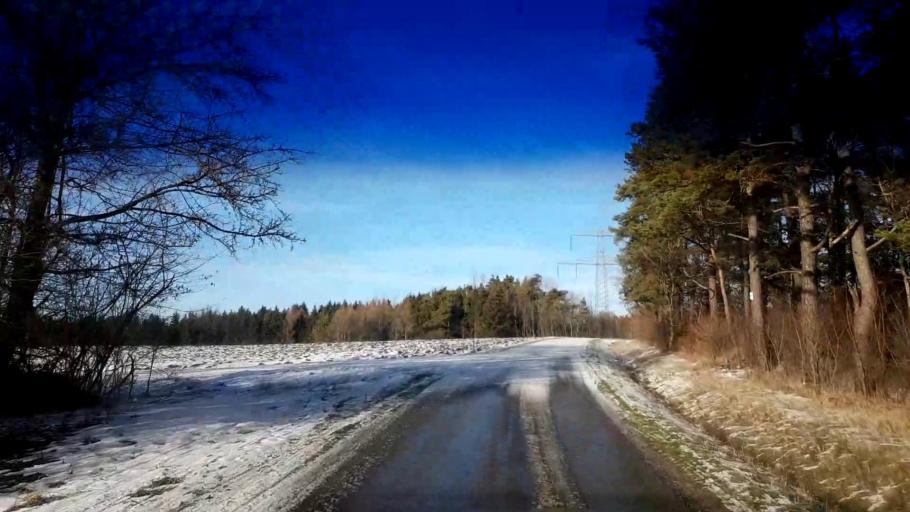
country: DE
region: Bavaria
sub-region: Upper Franconia
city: Heiligenstadt
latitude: 49.8425
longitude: 11.1038
